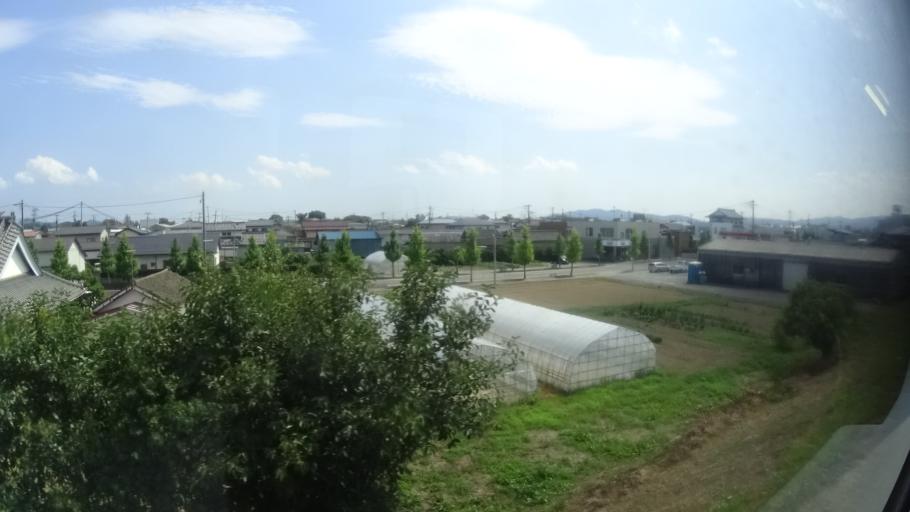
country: JP
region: Miyagi
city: Wakuya
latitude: 38.5837
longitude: 141.2489
